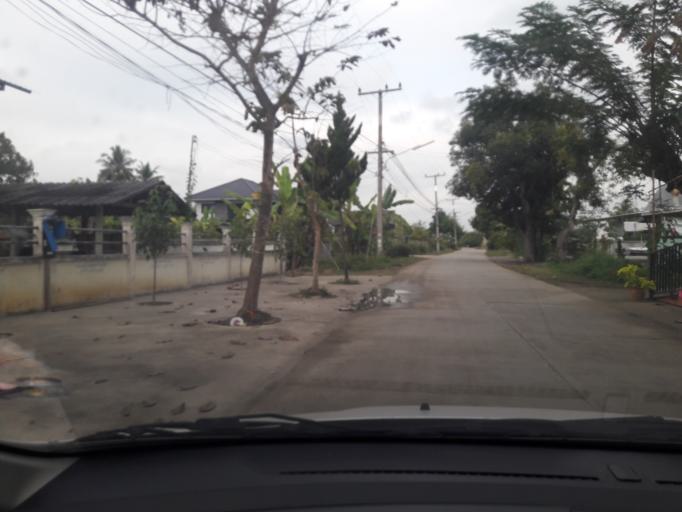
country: TH
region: Chiang Mai
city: Saraphi
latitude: 18.7199
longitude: 99.0584
